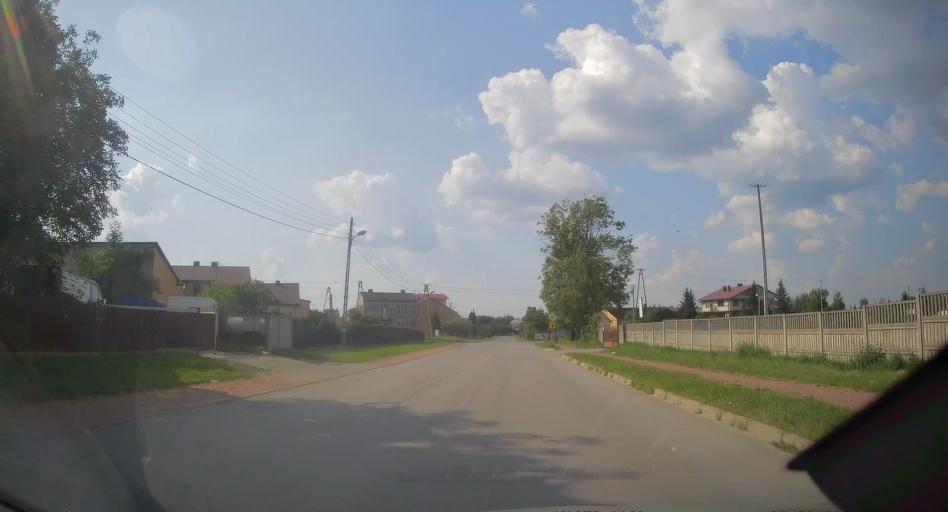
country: PL
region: Swietokrzyskie
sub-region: Powiat konecki
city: Radoszyce
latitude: 51.0774
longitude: 20.2560
